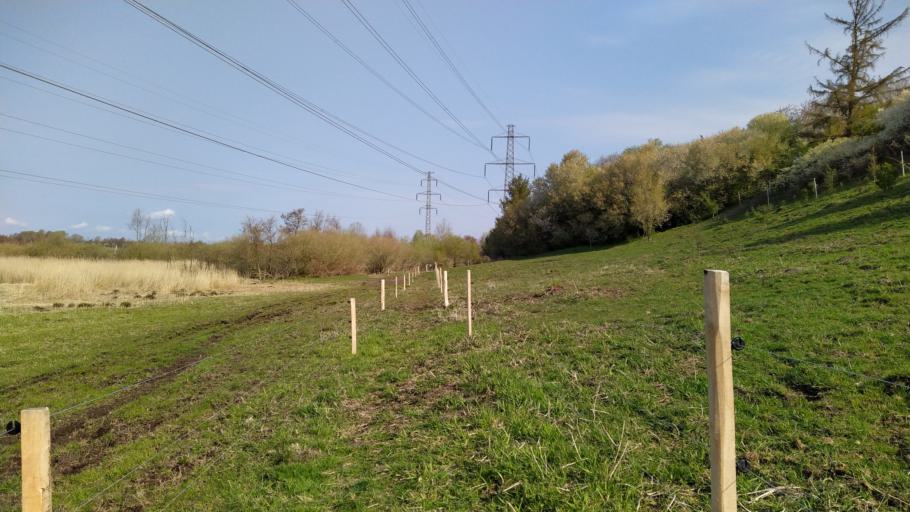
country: DK
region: Capital Region
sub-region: Egedal Kommune
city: Vekso
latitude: 55.7503
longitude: 12.2143
